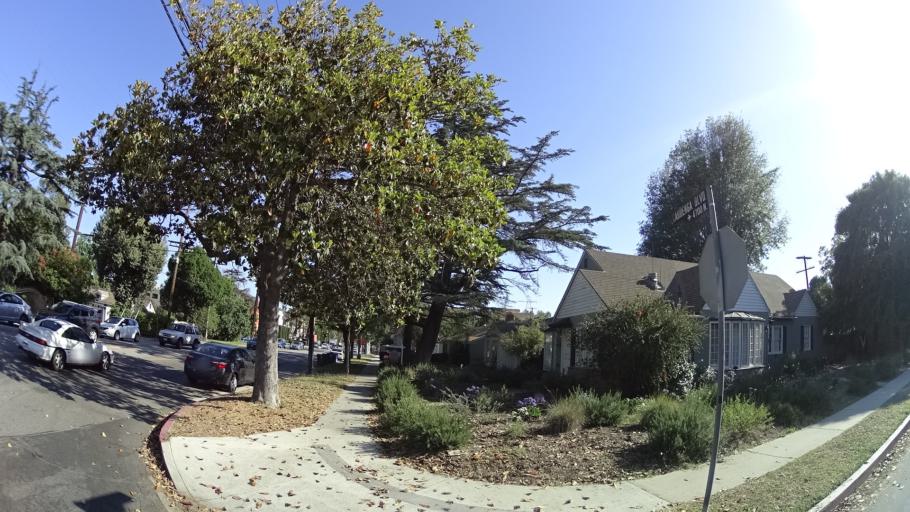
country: US
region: California
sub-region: Los Angeles County
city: Universal City
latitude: 34.1567
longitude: -118.3617
